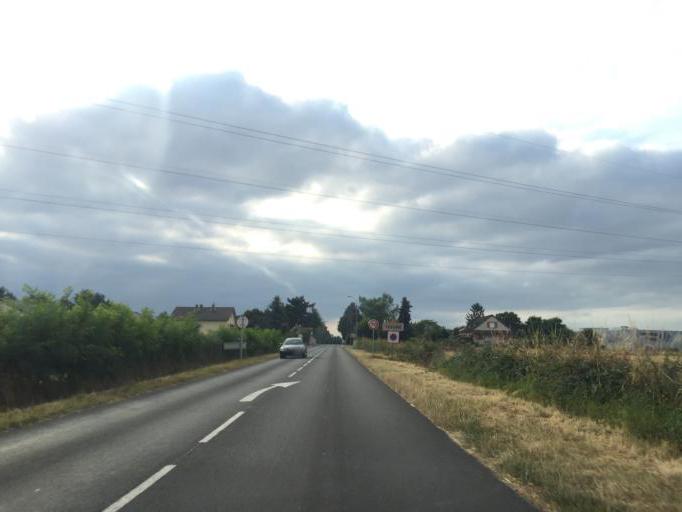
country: FR
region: Auvergne
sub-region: Departement de l'Allier
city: Yzeure
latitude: 46.5497
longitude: 3.3705
